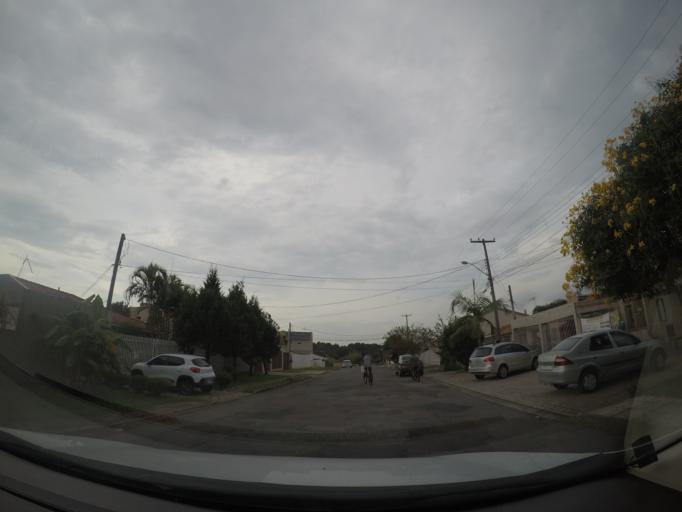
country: BR
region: Parana
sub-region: Sao Jose Dos Pinhais
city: Sao Jose dos Pinhais
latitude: -25.5113
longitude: -49.2408
